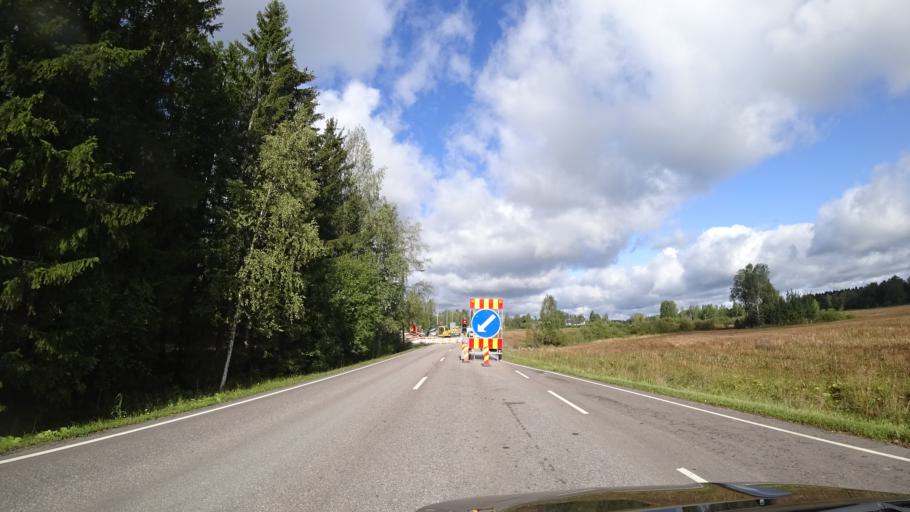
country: FI
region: Uusimaa
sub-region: Helsinki
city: Hyvinge
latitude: 60.6469
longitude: 25.0009
